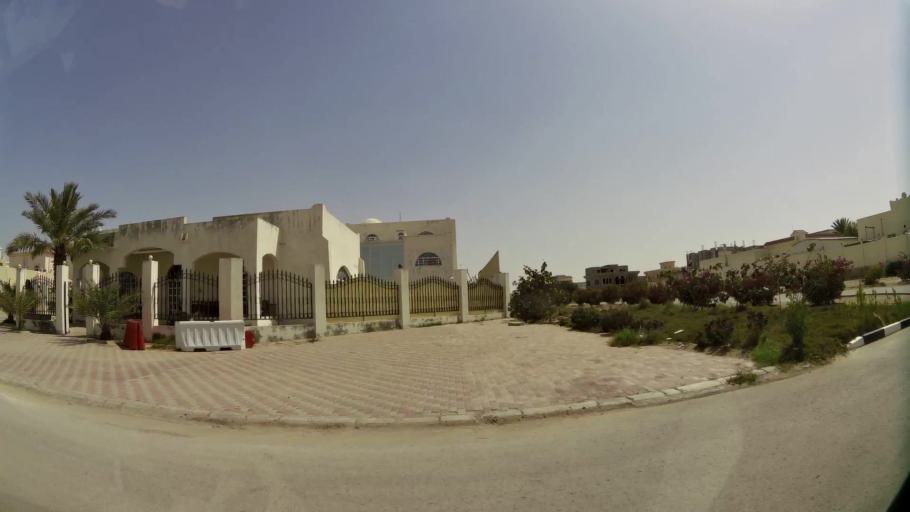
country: QA
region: Baladiyat Umm Salal
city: Umm Salal Muhammad
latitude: 25.3833
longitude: 51.4187
